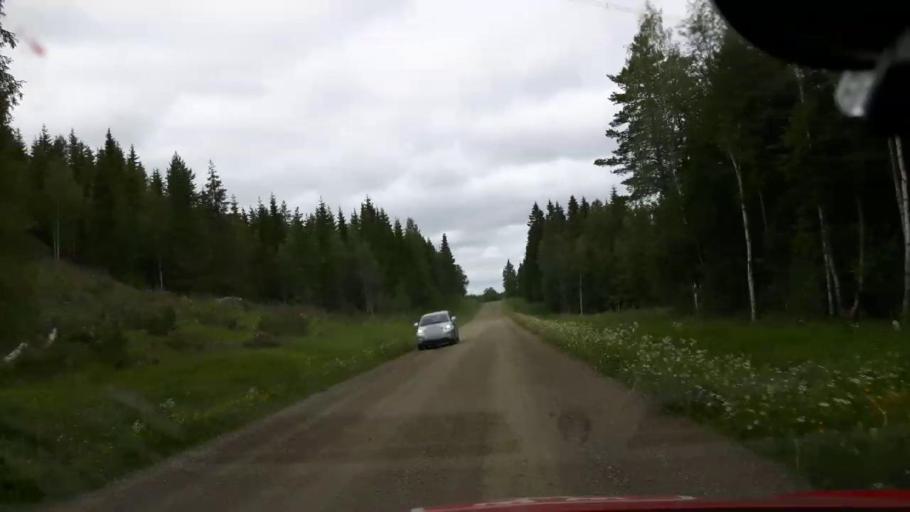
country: SE
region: Jaemtland
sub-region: OEstersunds Kommun
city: Brunflo
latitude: 62.9410
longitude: 14.9893
